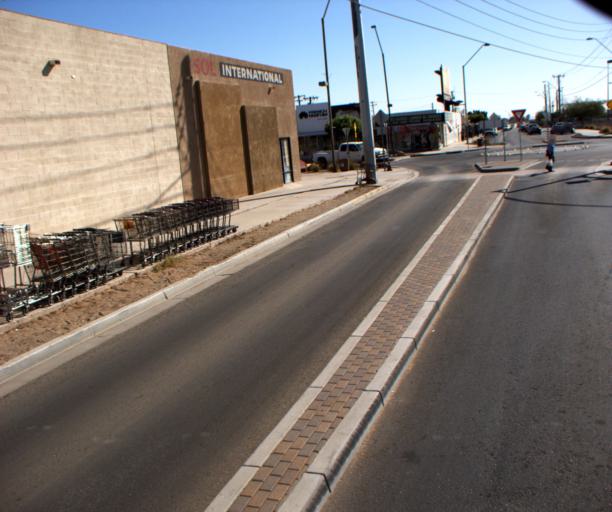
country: US
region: Arizona
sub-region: Yuma County
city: San Luis
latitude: 32.4870
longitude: -114.7828
